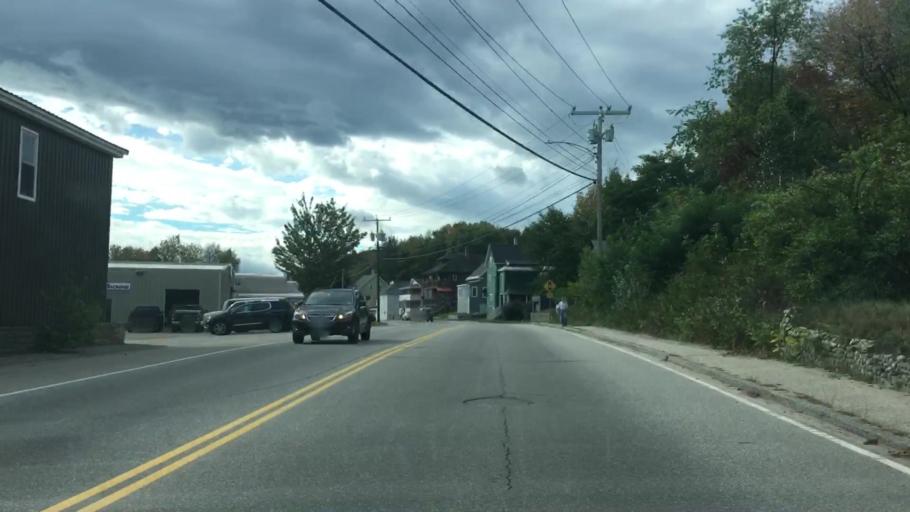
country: US
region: New Hampshire
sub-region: Coos County
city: Berlin
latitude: 44.4636
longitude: -71.1861
